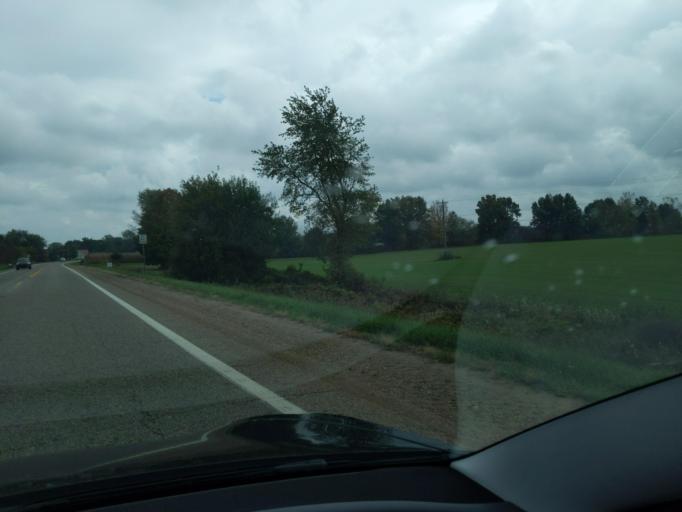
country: US
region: Michigan
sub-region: Eaton County
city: Charlotte
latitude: 42.5531
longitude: -84.7653
